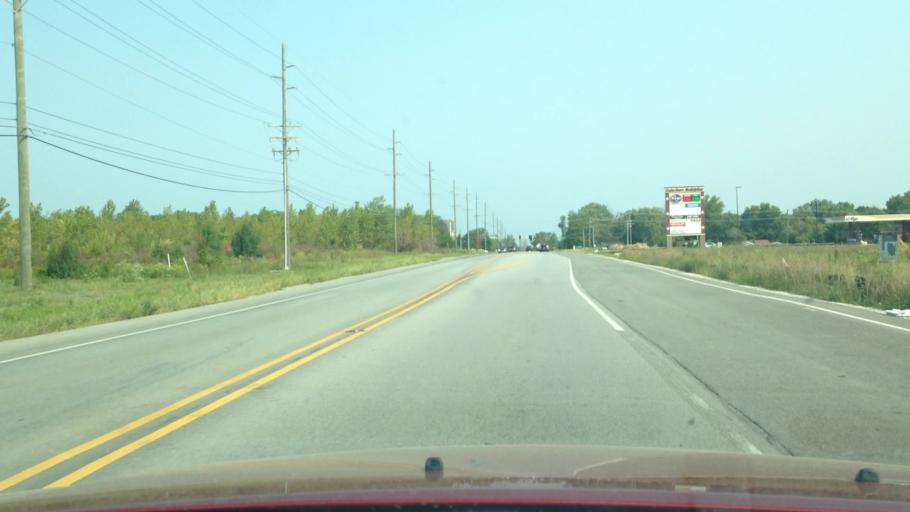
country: US
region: Indiana
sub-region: Johnson County
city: Waterloo
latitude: 39.5595
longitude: -86.1588
